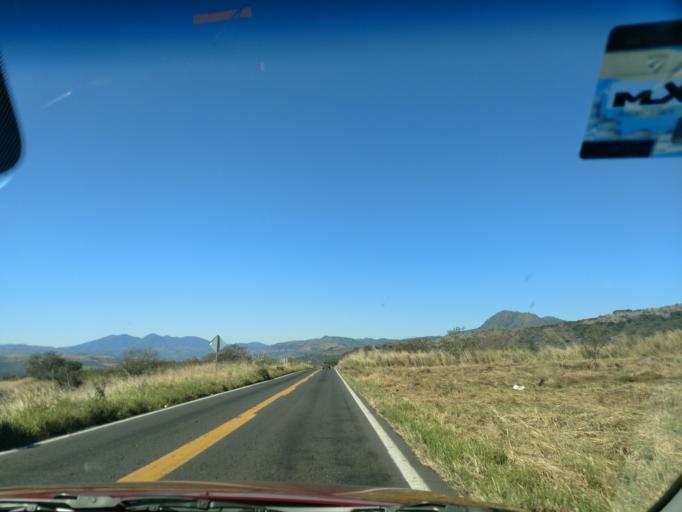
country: MX
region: Nayarit
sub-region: Ahuacatlan
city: Ahuacatlan
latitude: 21.0978
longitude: -104.5838
